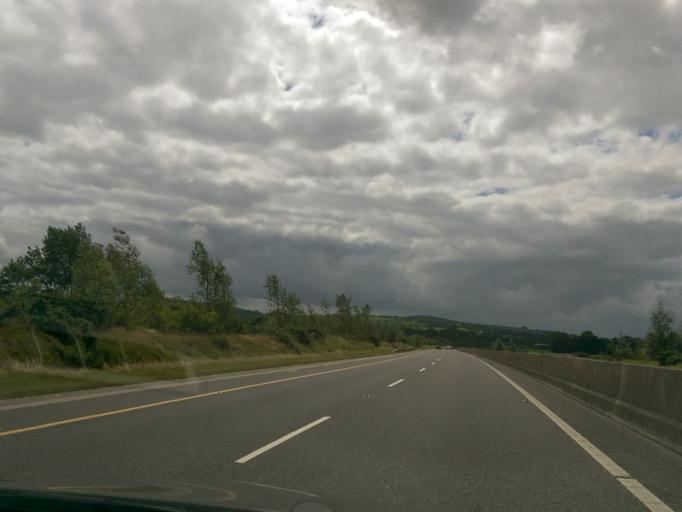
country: IE
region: Munster
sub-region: County Cork
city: Mitchelstown
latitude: 52.2637
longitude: -8.2483
